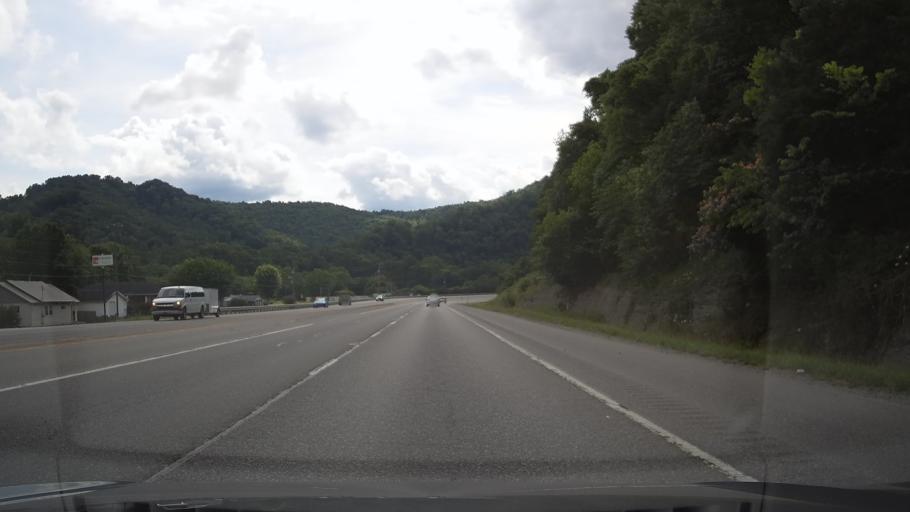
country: US
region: Kentucky
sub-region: Pike County
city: Coal Run Village
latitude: 37.5748
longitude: -82.6539
